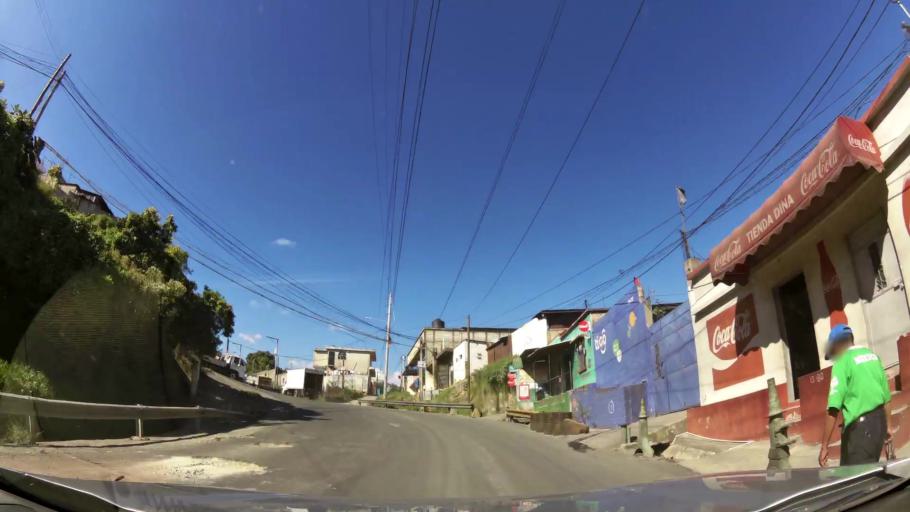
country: GT
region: Guatemala
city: Villa Nueva
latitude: 14.5501
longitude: -90.6190
